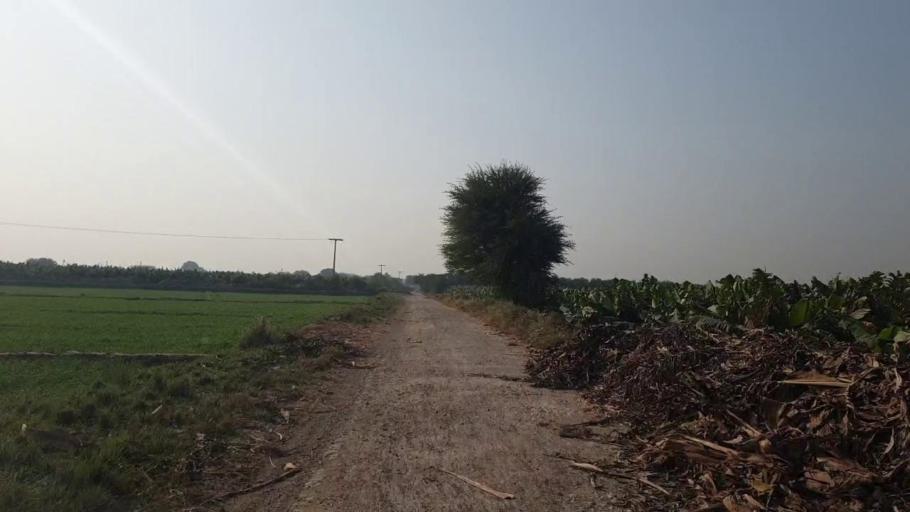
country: PK
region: Sindh
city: Kotri
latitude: 25.3442
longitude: 68.3230
